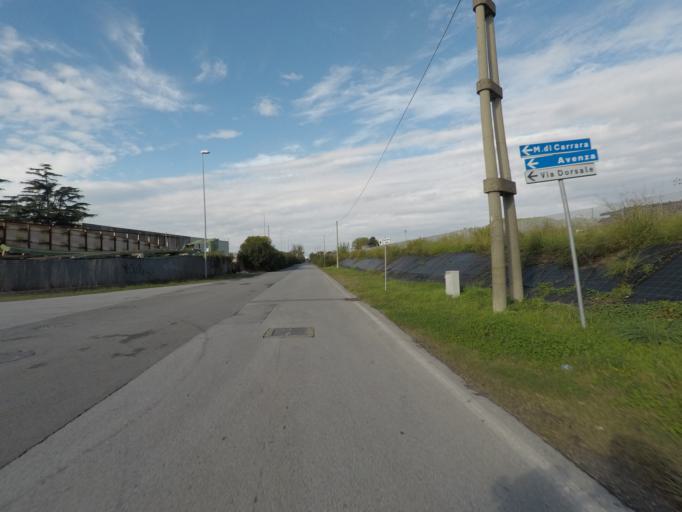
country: IT
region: Tuscany
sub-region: Provincia di Massa-Carrara
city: Massa
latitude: 44.0318
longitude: 10.1048
